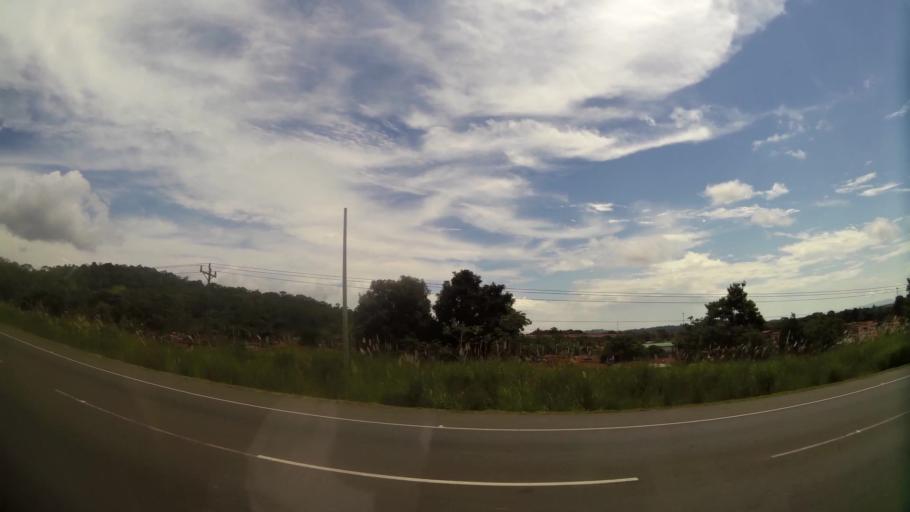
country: PA
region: Panama
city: Vista Alegre
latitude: 8.9272
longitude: -79.6933
